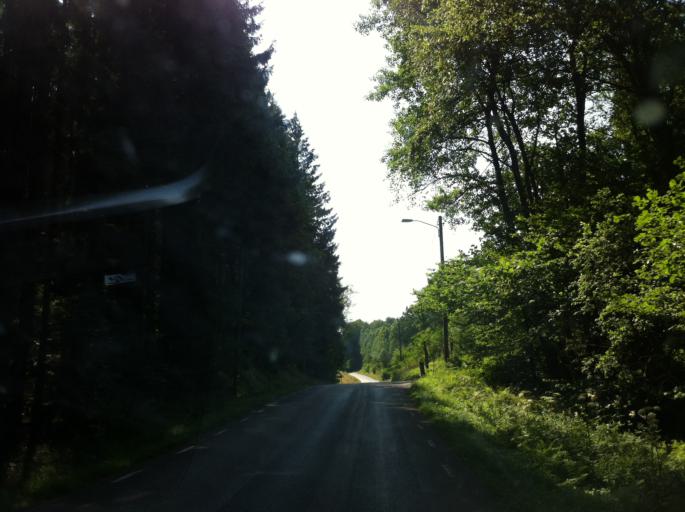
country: SE
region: Skane
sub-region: Hoors Kommun
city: Hoeoer
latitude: 56.0146
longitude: 13.4990
